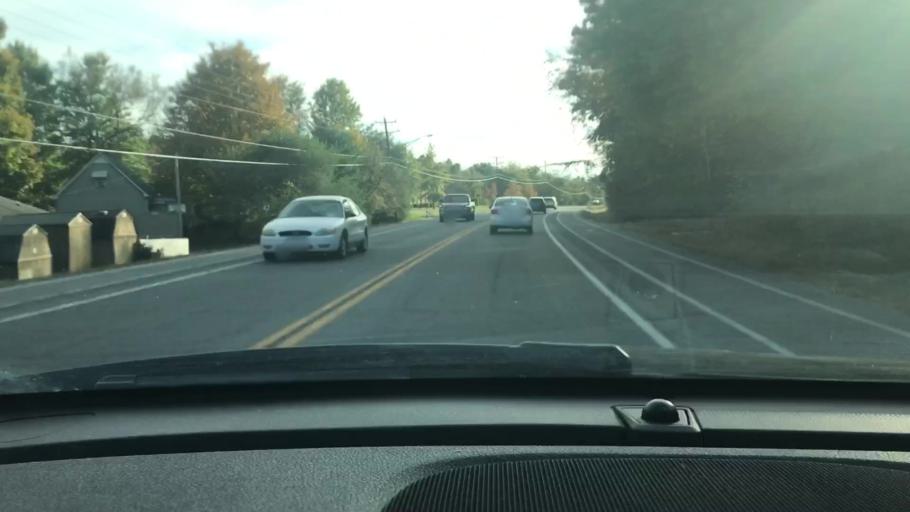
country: US
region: Tennessee
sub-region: Sumner County
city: White House
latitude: 36.4386
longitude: -86.6809
